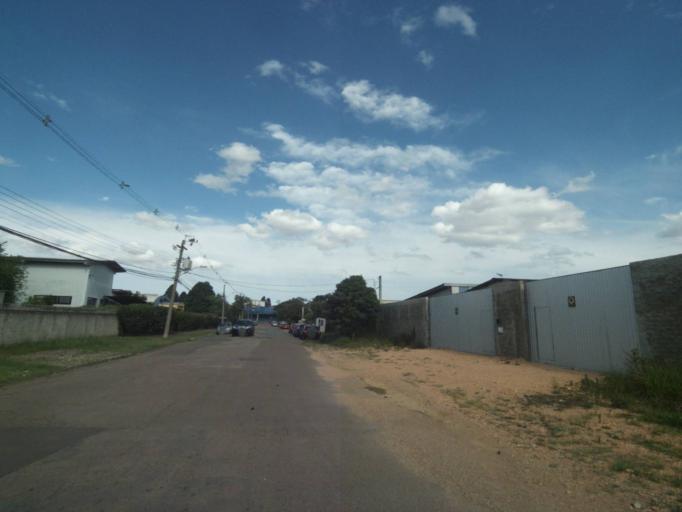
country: BR
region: Parana
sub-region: Curitiba
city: Curitiba
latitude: -25.4968
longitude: -49.3325
